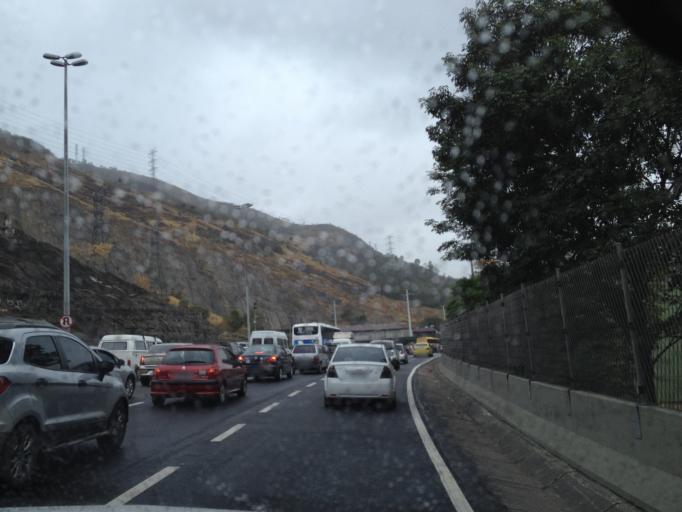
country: BR
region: Rio de Janeiro
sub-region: Rio De Janeiro
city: Rio de Janeiro
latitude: -22.9063
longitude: -43.3059
